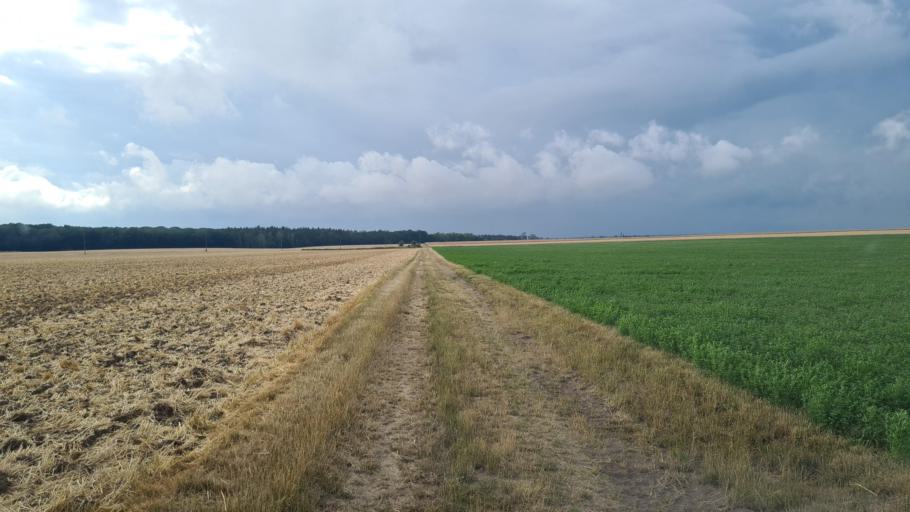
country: DE
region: Brandenburg
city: Juterbog
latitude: 51.9332
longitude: 13.1139
